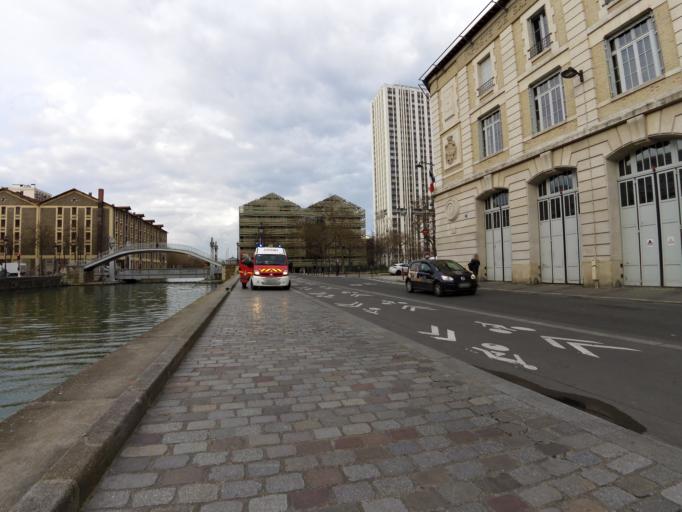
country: FR
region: Ile-de-France
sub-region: Departement de Seine-Saint-Denis
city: Le Pre-Saint-Gervais
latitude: 48.8889
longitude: 2.3801
